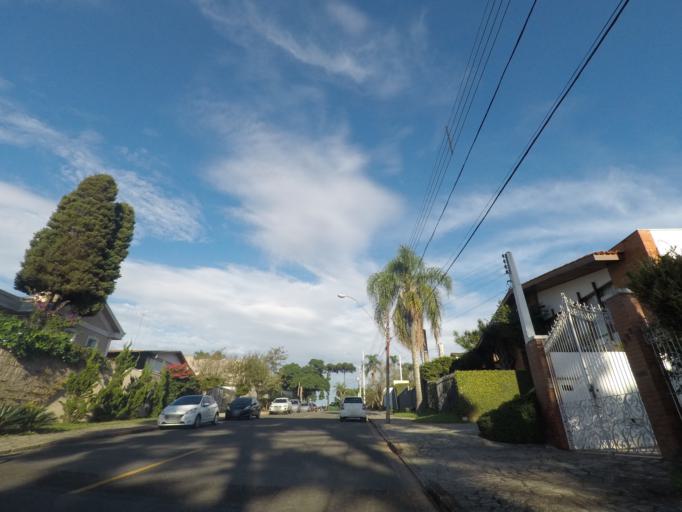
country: BR
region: Parana
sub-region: Curitiba
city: Curitiba
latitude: -25.4524
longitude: -49.3085
